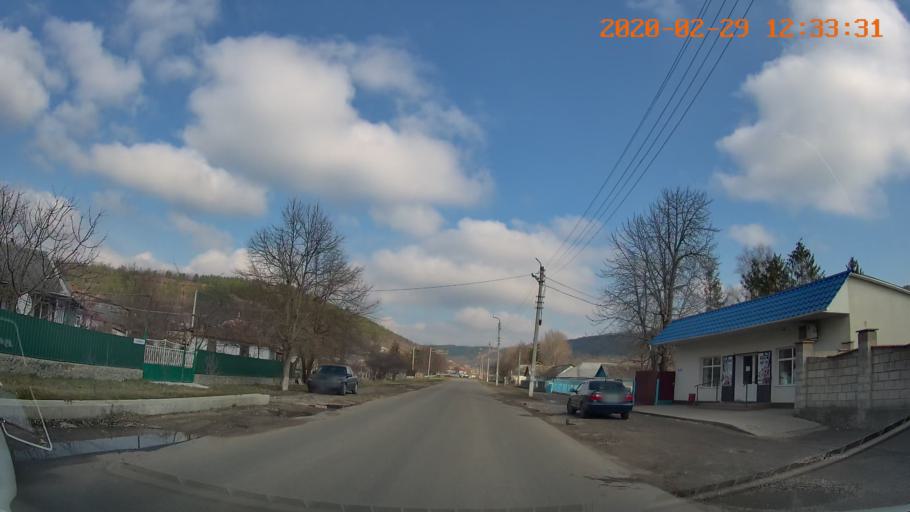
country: MD
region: Telenesti
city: Camenca
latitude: 48.0356
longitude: 28.7050
